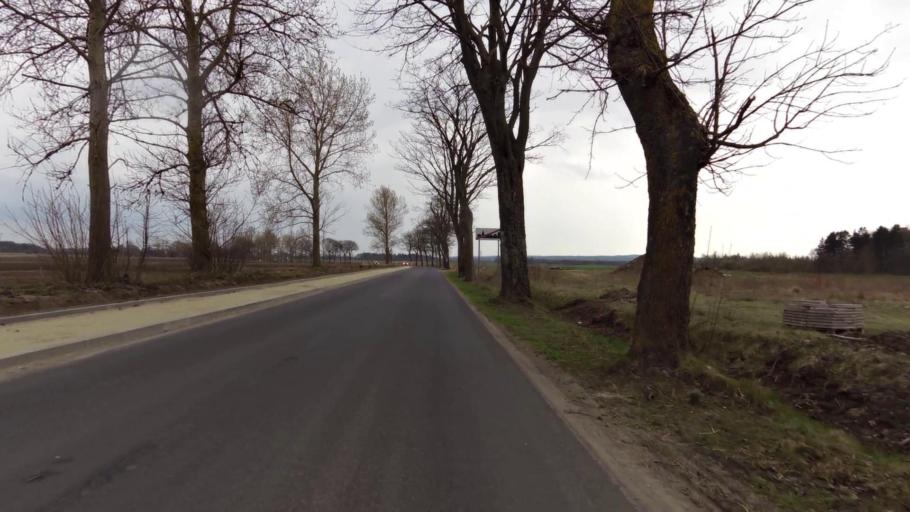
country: PL
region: West Pomeranian Voivodeship
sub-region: Powiat koszalinski
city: Sianow
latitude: 54.2781
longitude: 16.2215
